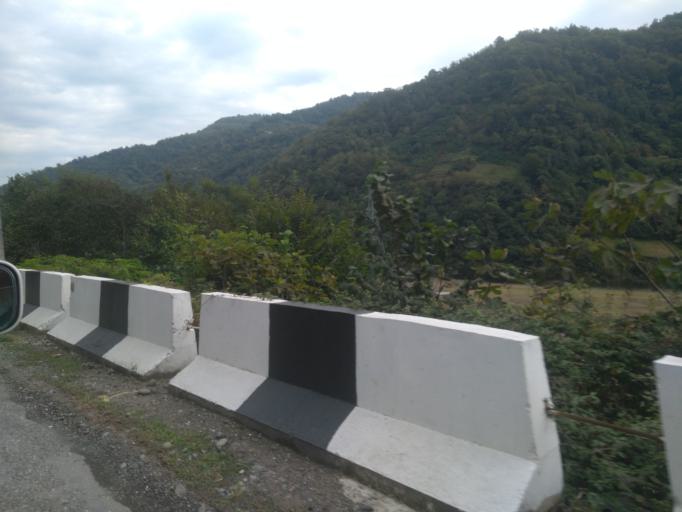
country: TR
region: Artvin
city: Muratli
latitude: 41.5459
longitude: 41.7897
